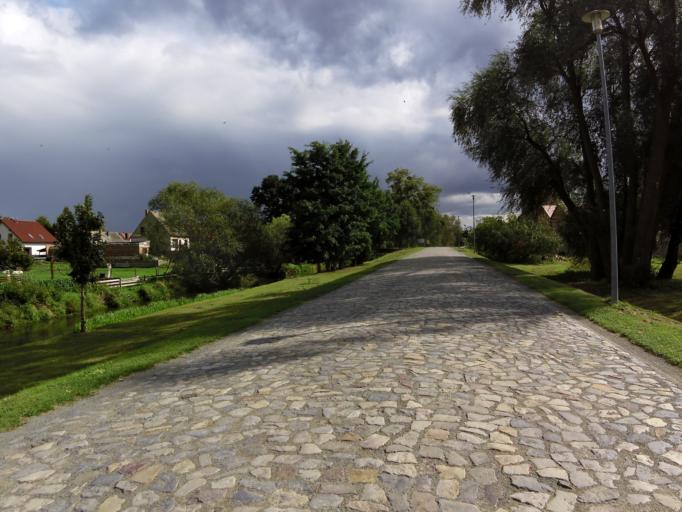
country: DE
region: Saxony-Anhalt
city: Barby
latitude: 51.9654
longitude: 11.9355
